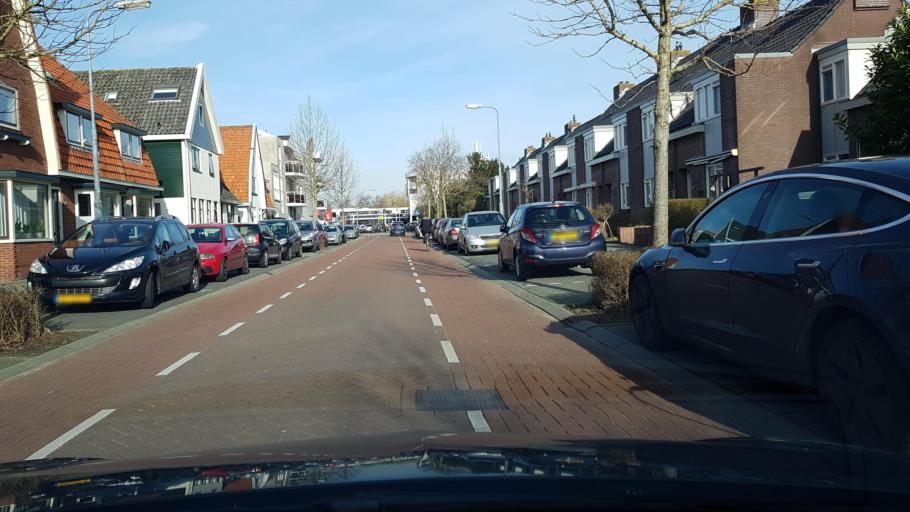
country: NL
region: North Holland
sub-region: Gemeente Zaanstad
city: Zaanstad
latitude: 52.4975
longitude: 4.8125
